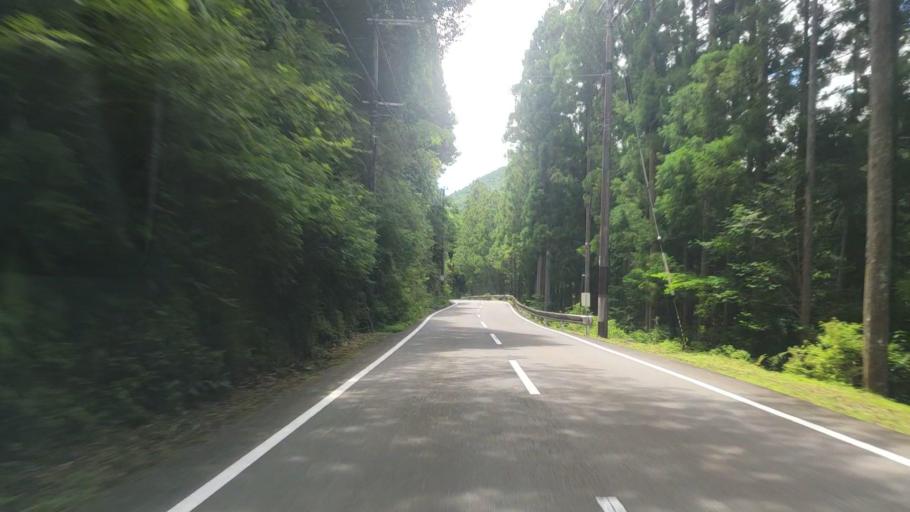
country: JP
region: Mie
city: Owase
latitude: 33.9685
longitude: 136.0616
